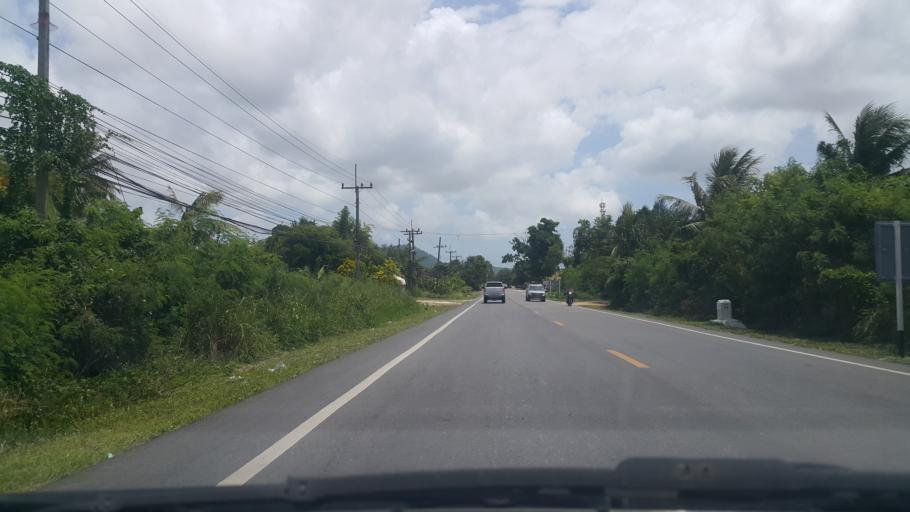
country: TH
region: Rayong
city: Ban Chang
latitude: 12.7596
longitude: 101.0275
